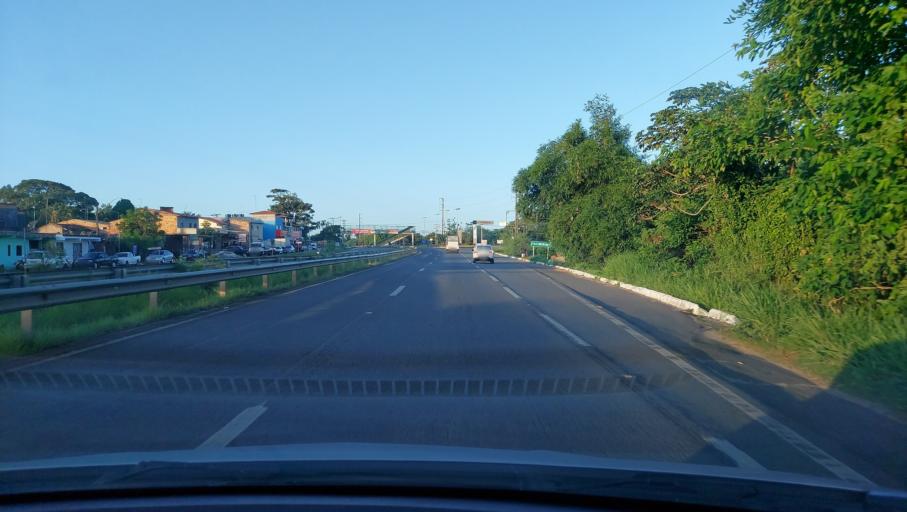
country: BR
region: Bahia
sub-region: Mata De Sao Joao
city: Mata de Sao Joao
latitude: -12.5973
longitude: -38.0438
